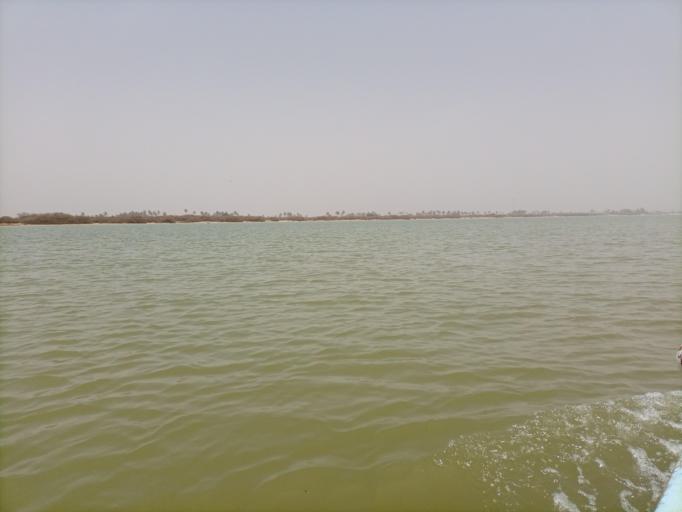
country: SN
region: Saint-Louis
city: Saint-Louis
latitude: 15.8560
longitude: -16.5172
